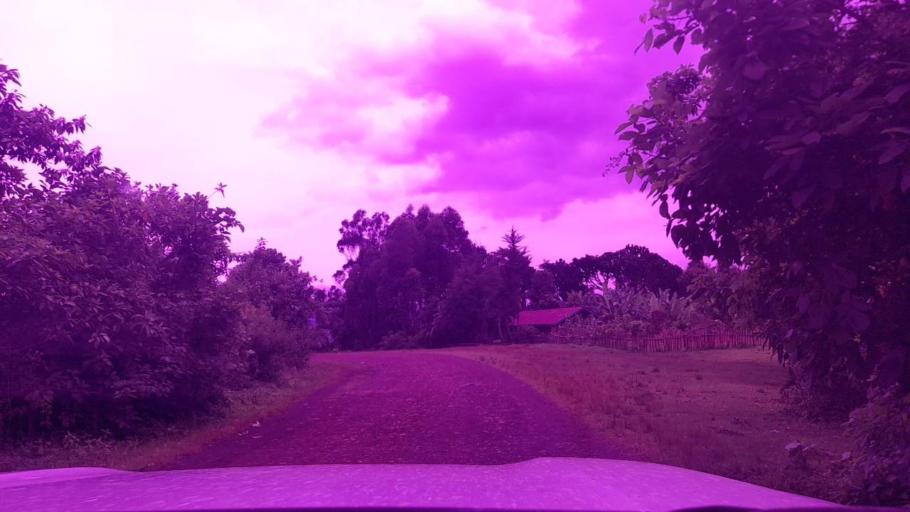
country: ET
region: Southern Nations, Nationalities, and People's Region
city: Tippi
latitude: 7.6338
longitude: 35.5764
